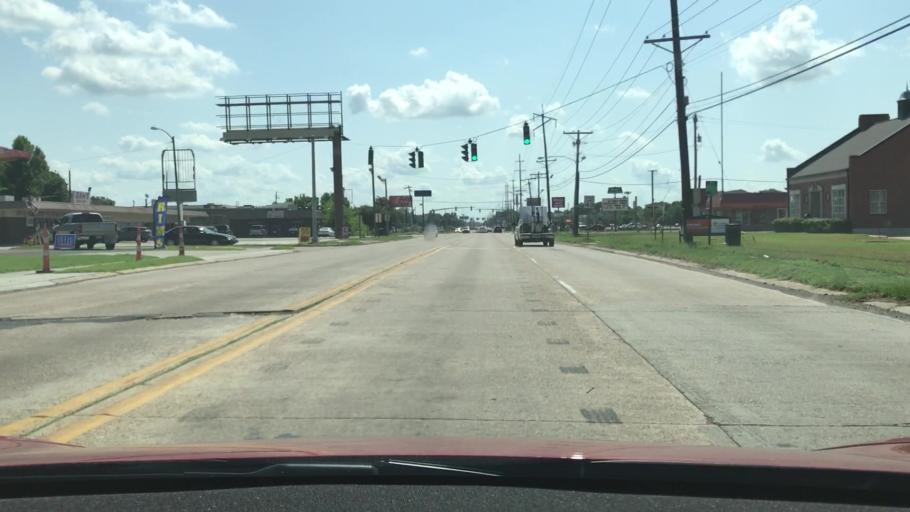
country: US
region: Louisiana
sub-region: Caddo Parish
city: Shreveport
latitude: 32.4420
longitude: -93.7862
